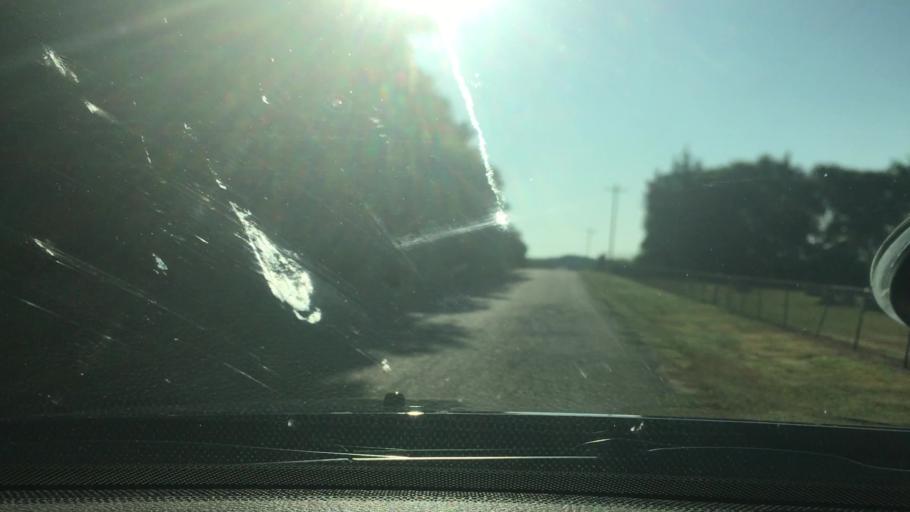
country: US
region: Oklahoma
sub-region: Murray County
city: Sulphur
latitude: 34.4049
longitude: -96.8077
